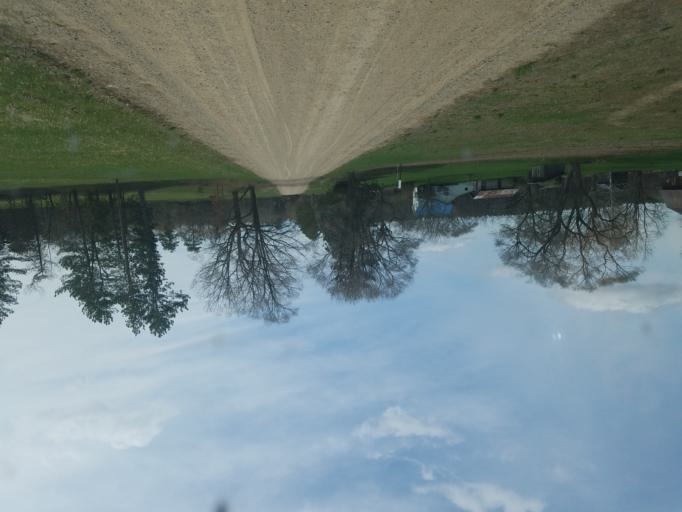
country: US
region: Michigan
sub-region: Isabella County
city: Lake Isabella
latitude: 43.5674
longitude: -84.9711
